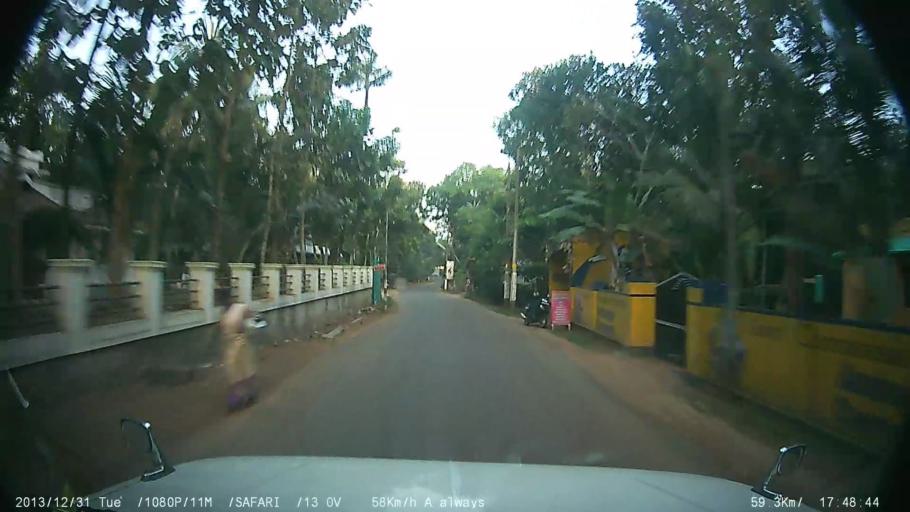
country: IN
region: Kerala
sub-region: Kottayam
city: Vaikam
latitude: 9.7466
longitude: 76.4811
